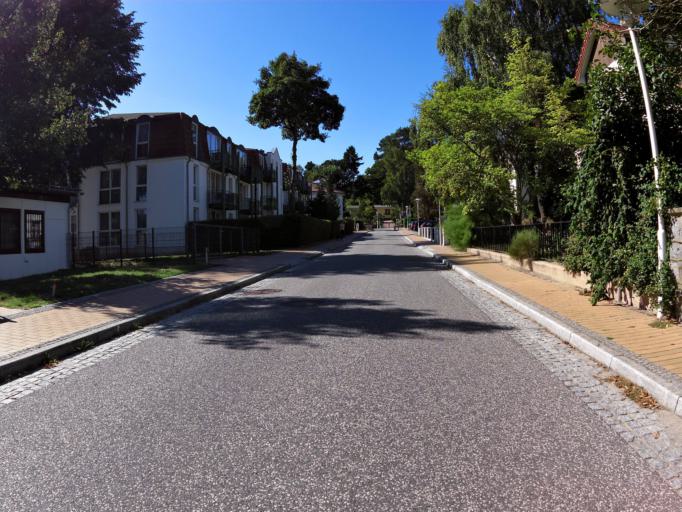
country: DE
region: Mecklenburg-Vorpommern
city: Seebad Bansin
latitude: 53.9703
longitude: 14.1394
